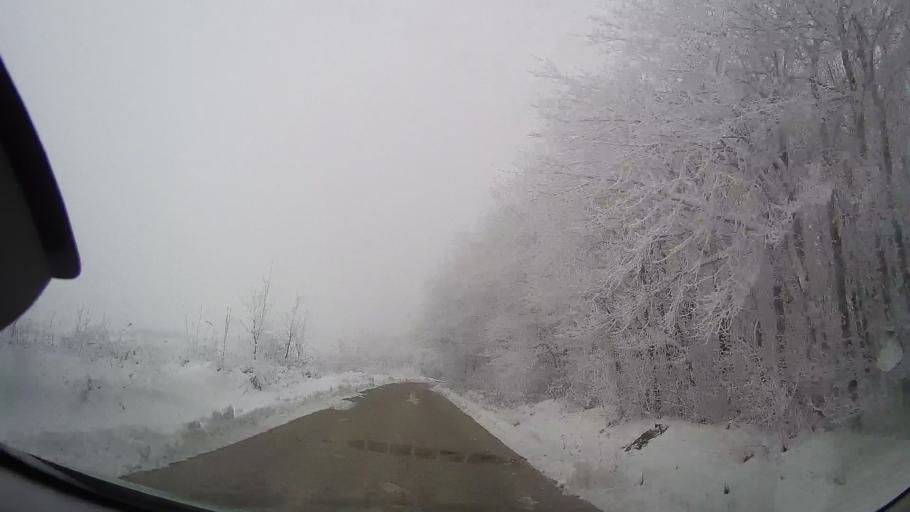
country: RO
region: Iasi
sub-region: Comuna Dagata
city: Dagata
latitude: 46.9151
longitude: 27.1819
